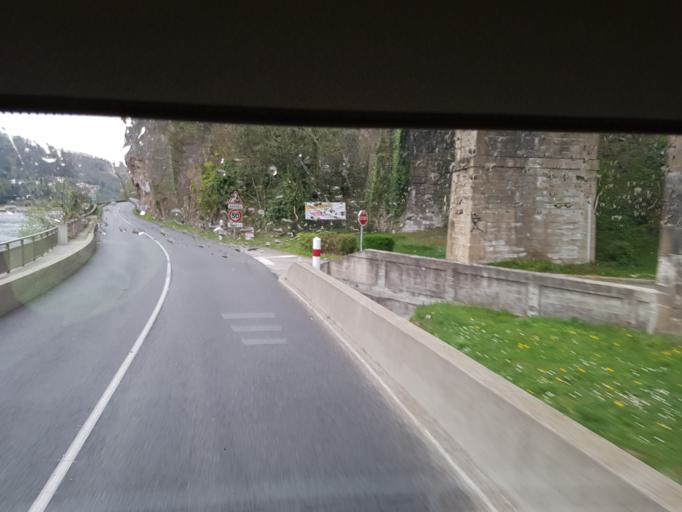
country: FR
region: Rhone-Alpes
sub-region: Departement de la Loire
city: Saint-Paul-en-Cornillon
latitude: 45.3967
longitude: 4.2356
